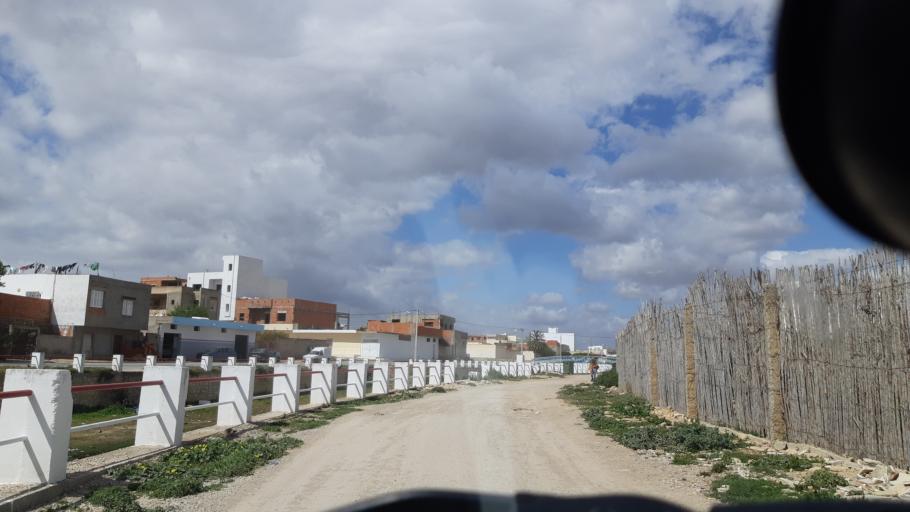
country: TN
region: Susah
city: Akouda
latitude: 35.8721
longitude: 10.5449
